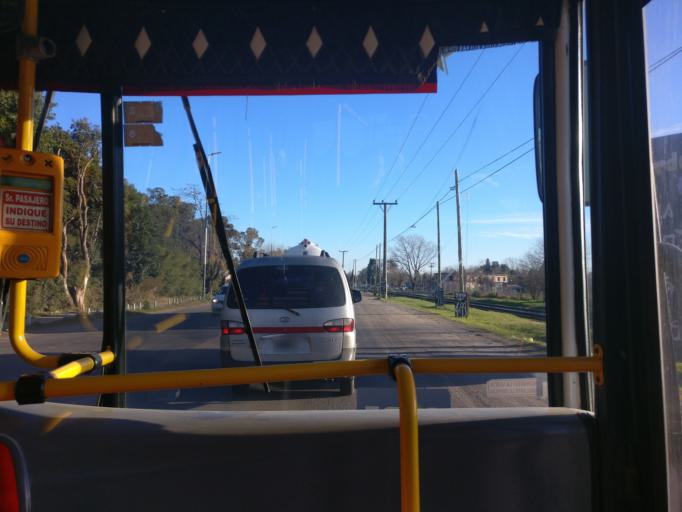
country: AR
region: Buenos Aires
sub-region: Partido de Ezeiza
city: Ezeiza
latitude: -34.9184
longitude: -58.6046
